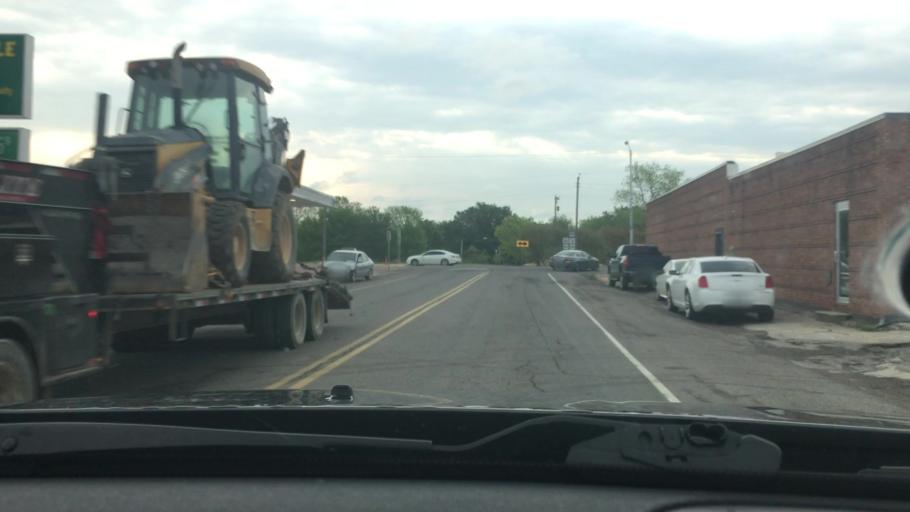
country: US
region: Oklahoma
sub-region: Coal County
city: Coalgate
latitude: 34.5406
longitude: -96.2188
